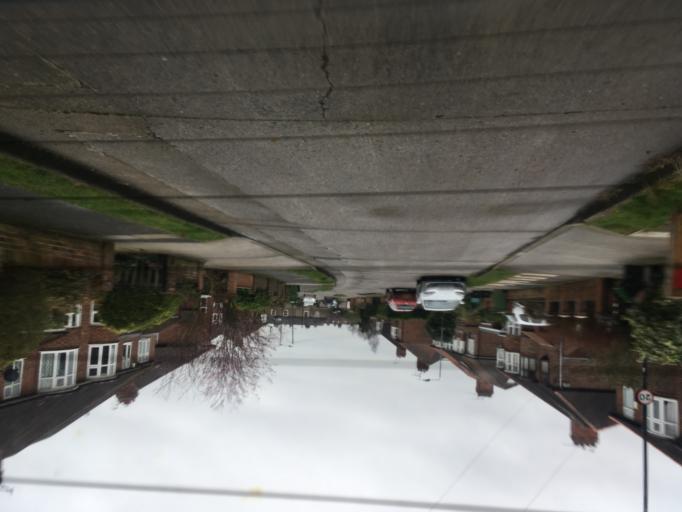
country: GB
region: England
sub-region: City of York
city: Heslington
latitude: 53.9686
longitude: -1.0595
